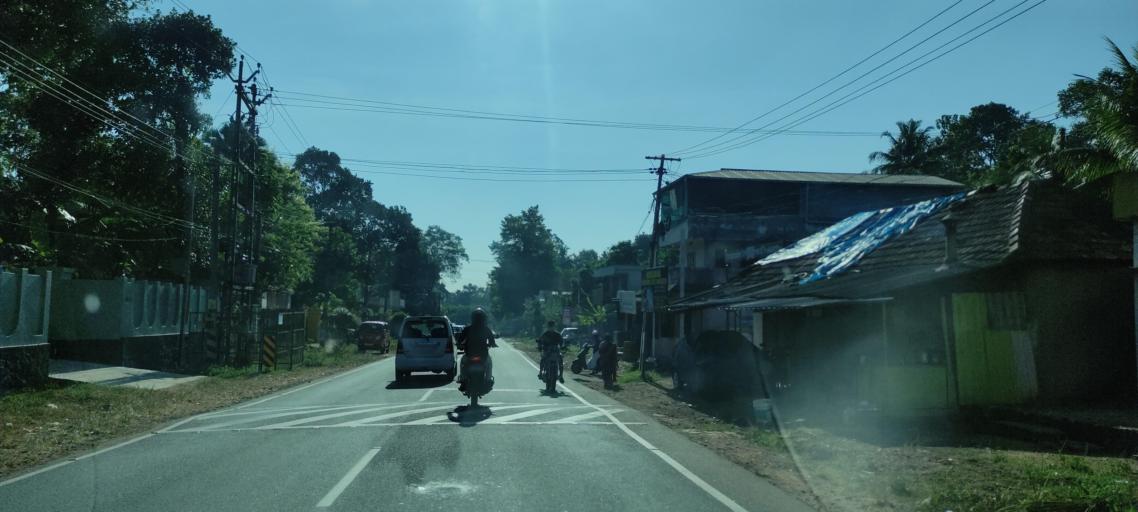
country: IN
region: Kerala
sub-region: Pattanamtitta
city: Adur
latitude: 9.1717
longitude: 76.6501
